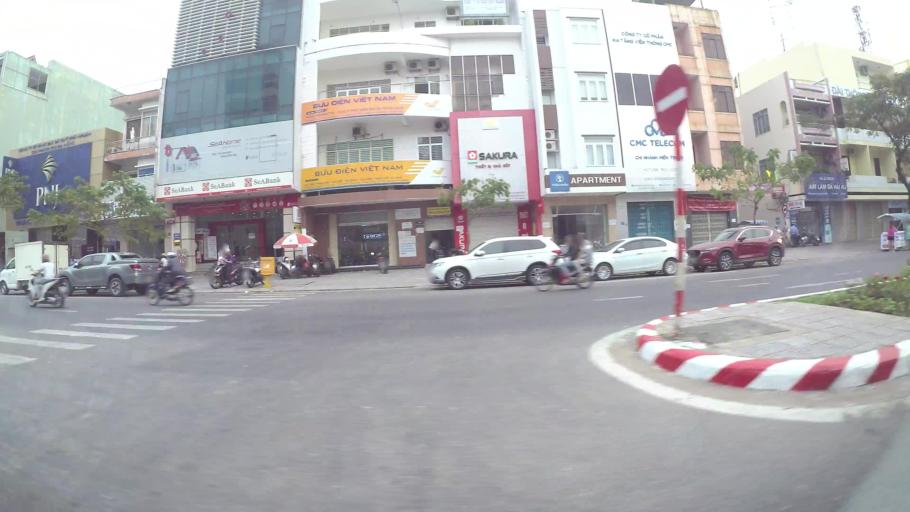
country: VN
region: Da Nang
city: Da Nang
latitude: 16.0592
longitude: 108.2074
